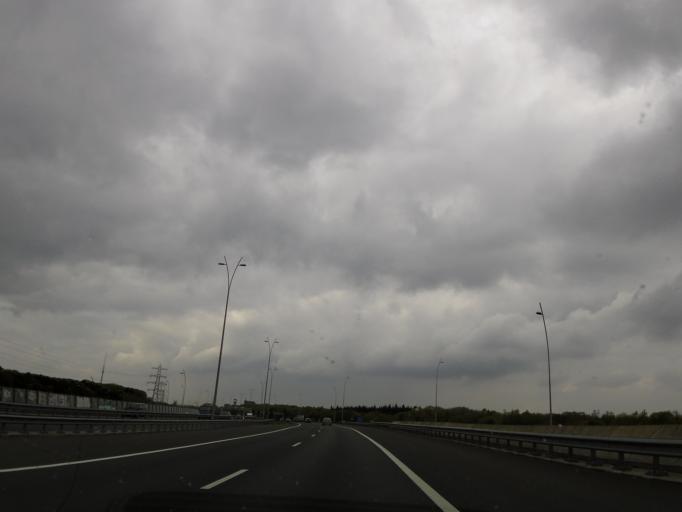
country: NL
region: North Brabant
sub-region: Gemeente Eindhoven
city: Lakerlopen
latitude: 51.4042
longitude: 5.4983
